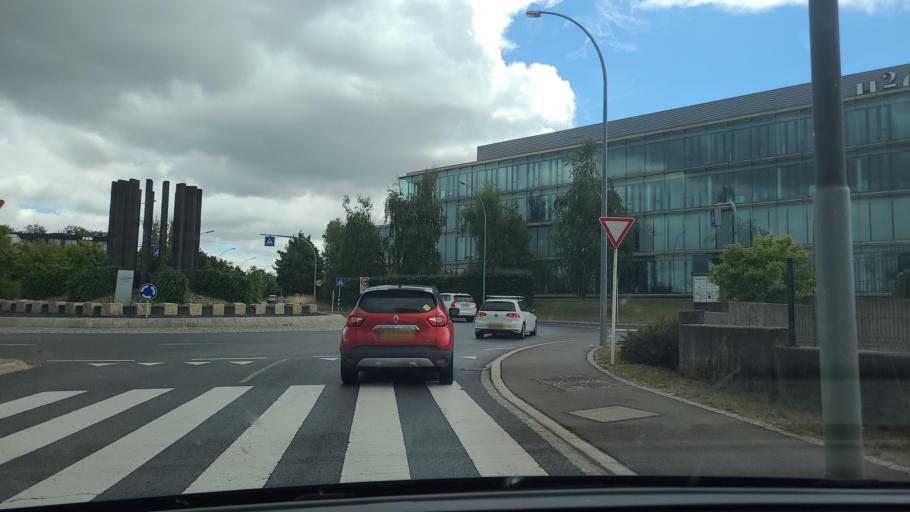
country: LU
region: Luxembourg
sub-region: Canton de Luxembourg
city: Hesperange
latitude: 49.5766
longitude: 6.1357
